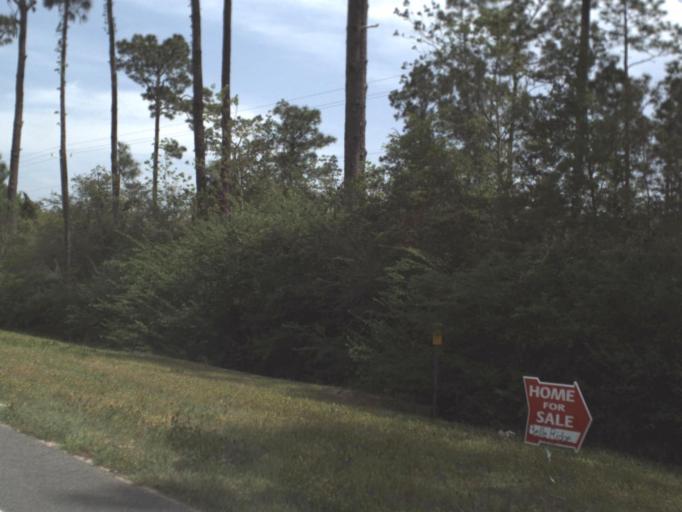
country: US
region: Florida
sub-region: Escambia County
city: Cantonment
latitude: 30.5351
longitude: -87.3590
